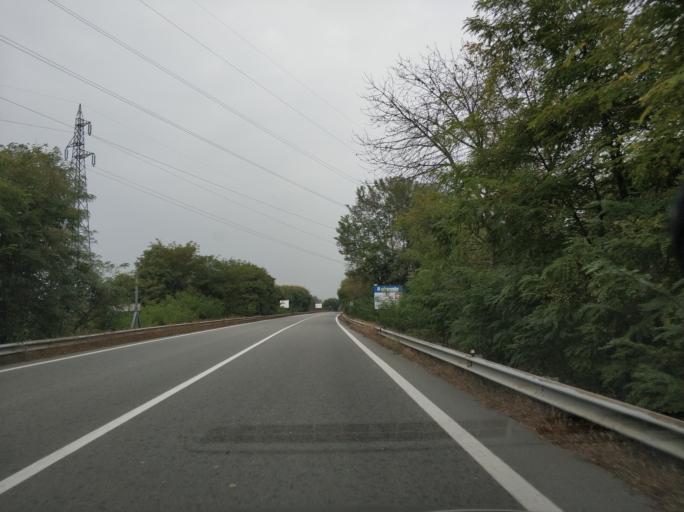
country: IT
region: Piedmont
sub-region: Provincia di Torino
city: Lombardore
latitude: 45.2382
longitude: 7.7453
